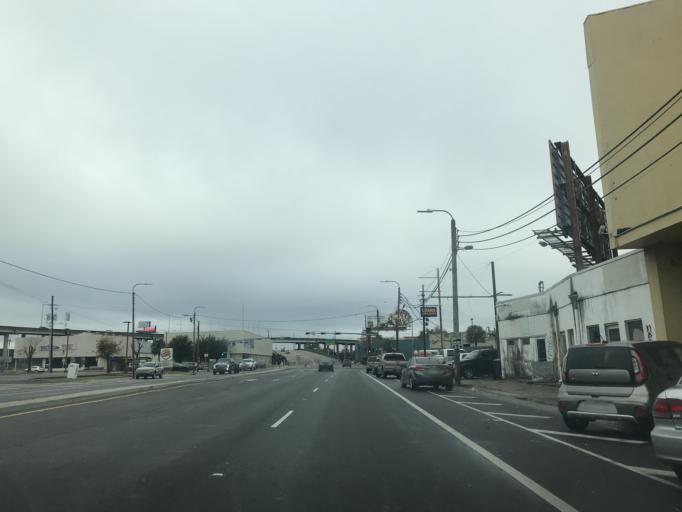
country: US
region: Louisiana
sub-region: Orleans Parish
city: New Orleans
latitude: 29.9686
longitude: -90.1054
